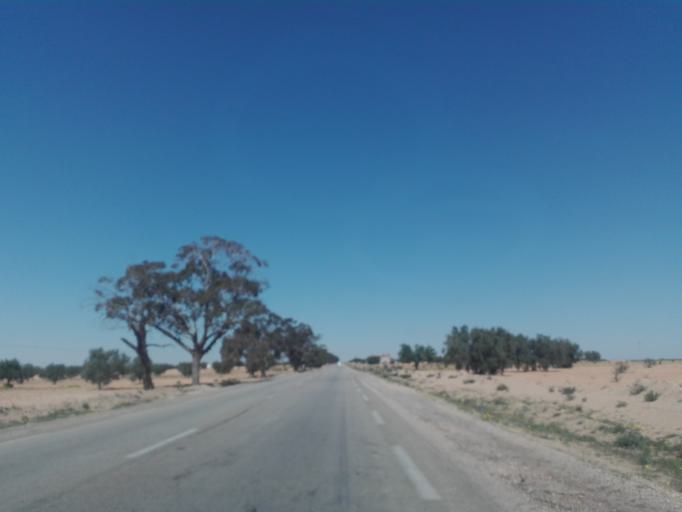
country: TN
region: Safaqis
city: Bi'r `Ali Bin Khalifah
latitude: 34.7521
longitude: 10.3421
